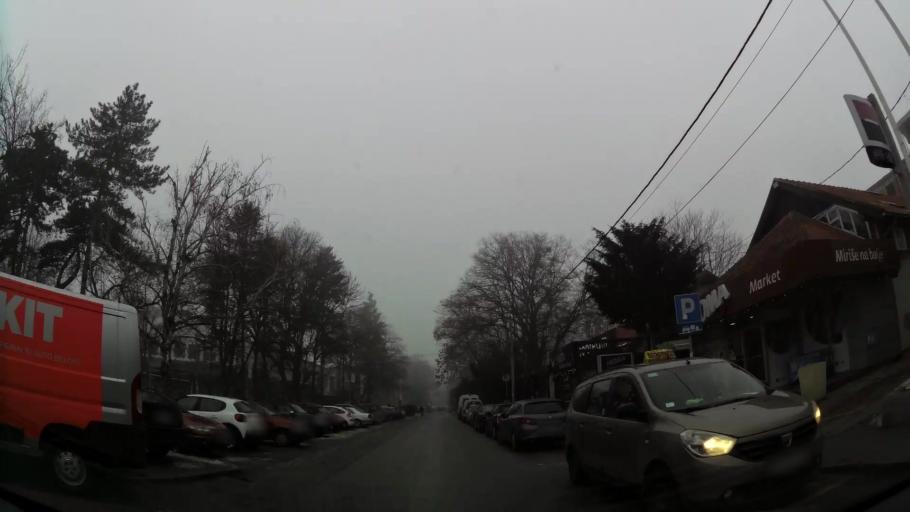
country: RS
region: Central Serbia
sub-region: Belgrade
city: Savski Venac
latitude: 44.7885
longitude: 20.4405
